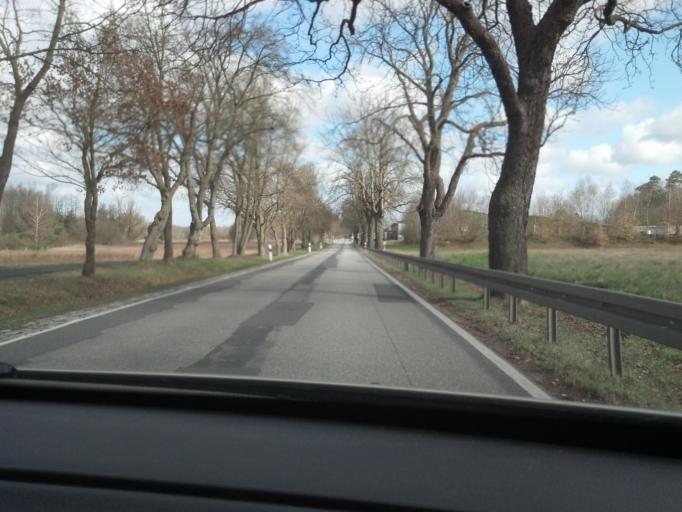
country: DE
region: Mecklenburg-Vorpommern
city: Boizenburg
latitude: 53.4131
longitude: 10.7420
